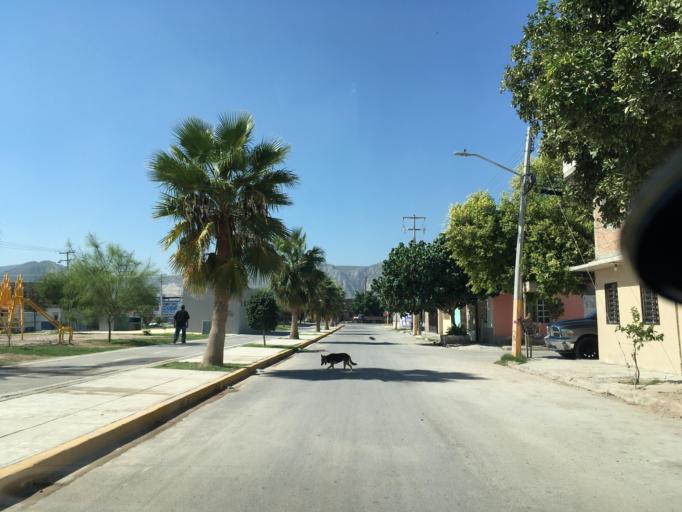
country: MX
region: Coahuila
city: Torreon
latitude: 25.5051
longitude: -103.3928
